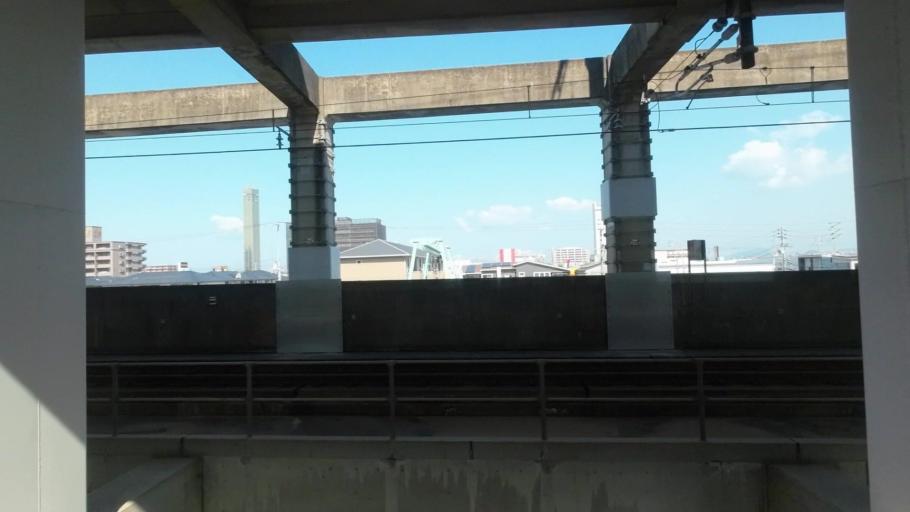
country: JP
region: Kagawa
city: Sakaidecho
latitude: 34.3110
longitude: 133.8169
